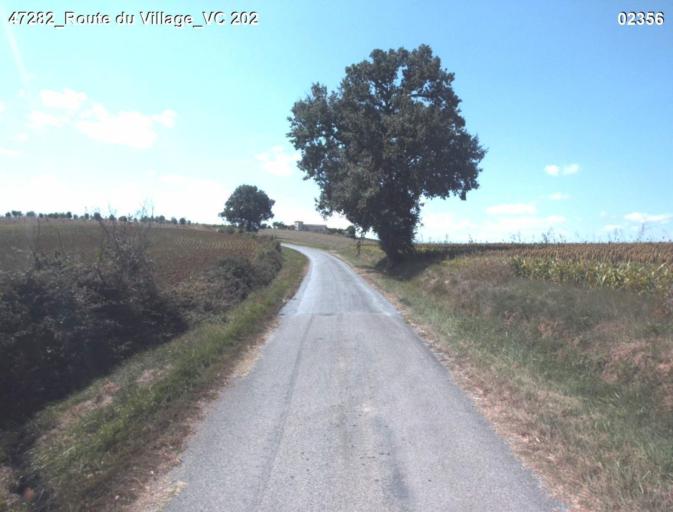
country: FR
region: Aquitaine
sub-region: Departement du Lot-et-Garonne
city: Laplume
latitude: 44.0907
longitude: 0.5259
